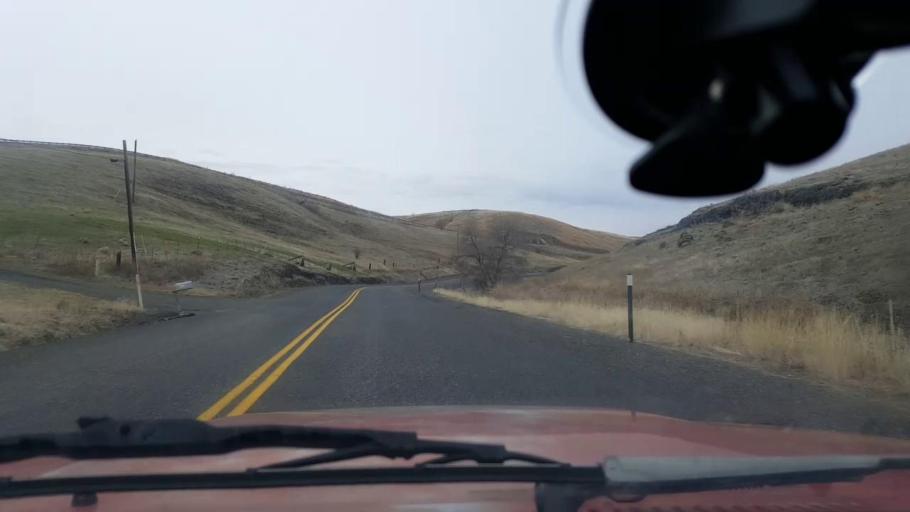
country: US
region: Washington
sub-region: Asotin County
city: Clarkston Heights-Vineland
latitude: 46.3835
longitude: -117.1342
